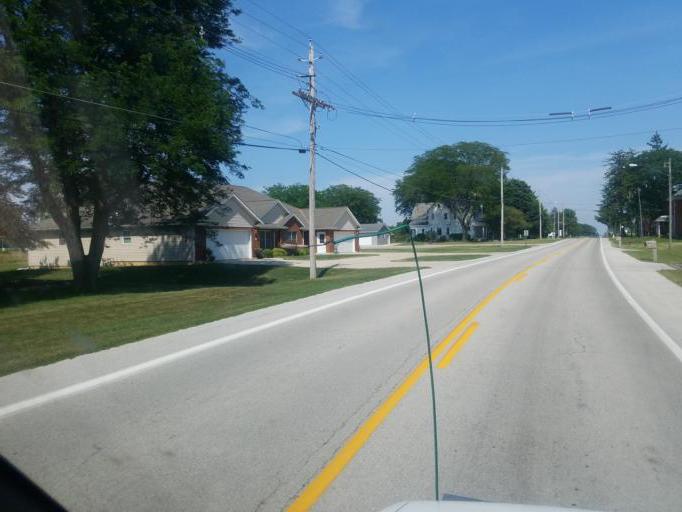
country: US
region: Ohio
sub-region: Auglaize County
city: New Bremen
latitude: 40.4959
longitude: -84.3123
